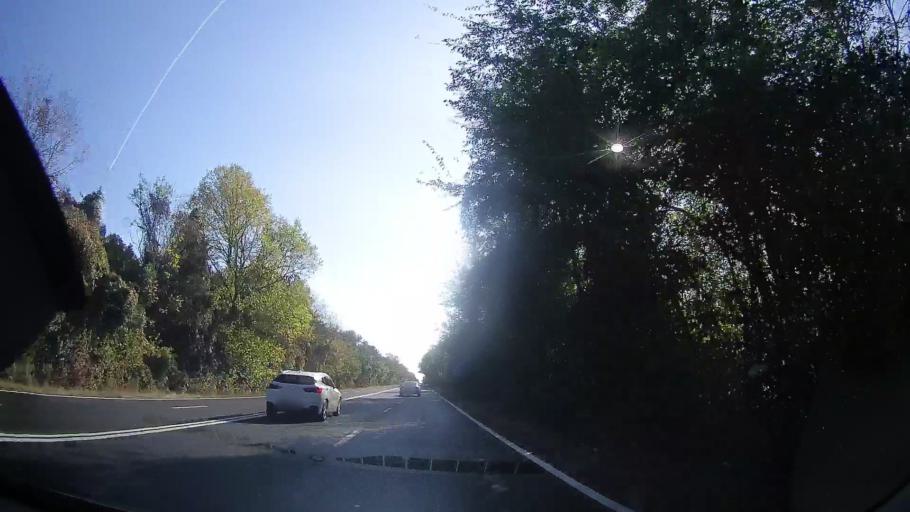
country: RO
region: Constanta
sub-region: Comuna Douazeci si Trei August
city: Dulcesti
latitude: 43.8718
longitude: 28.5744
